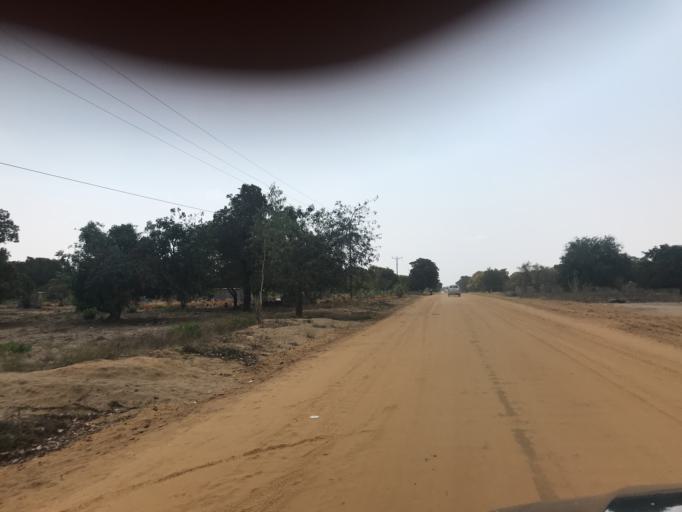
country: MZ
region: Gaza
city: Manjacaze
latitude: -24.5878
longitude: 33.9166
